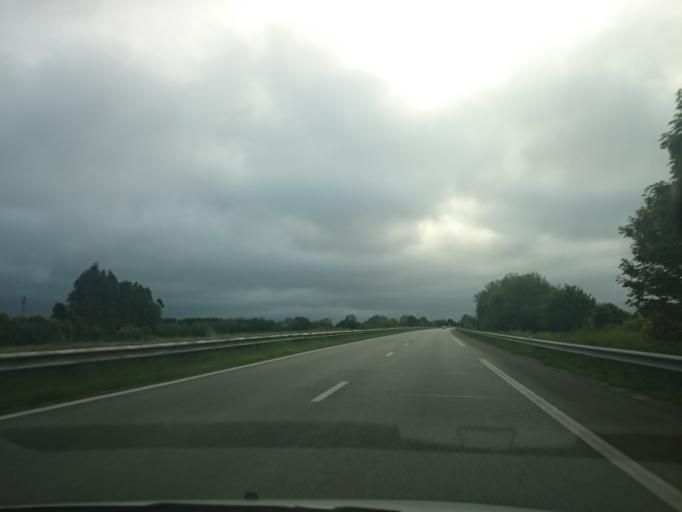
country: FR
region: Brittany
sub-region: Departement du Finistere
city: Saint-Yvi
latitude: 47.9429
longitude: -3.9278
